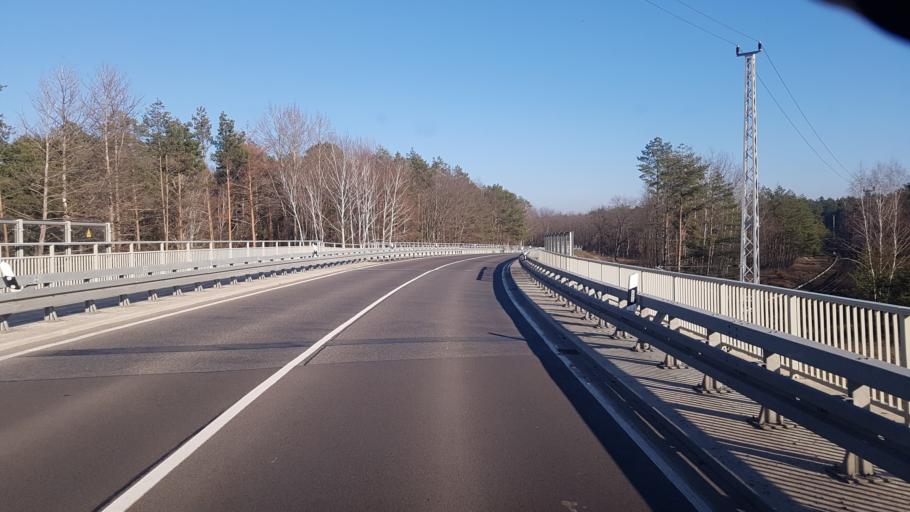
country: DE
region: Brandenburg
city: Doberlug-Kirchhain
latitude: 51.6304
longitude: 13.5904
